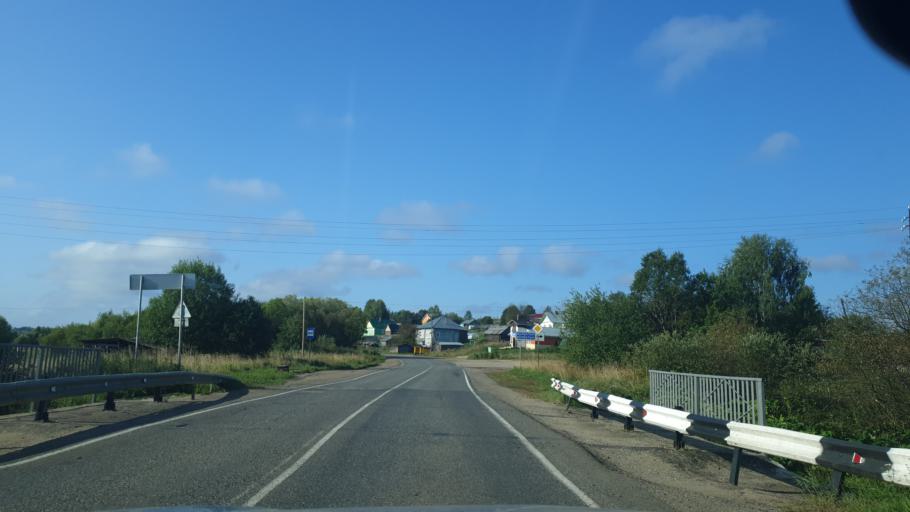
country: RU
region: Komi Republic
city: Vizinga
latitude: 60.9680
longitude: 50.2464
